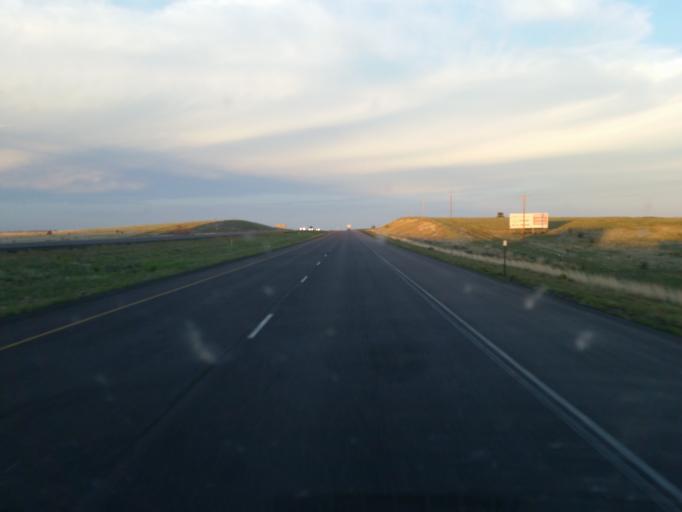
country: US
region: New Mexico
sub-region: Guadalupe County
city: Santa Rosa
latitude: 34.9900
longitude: -105.2656
